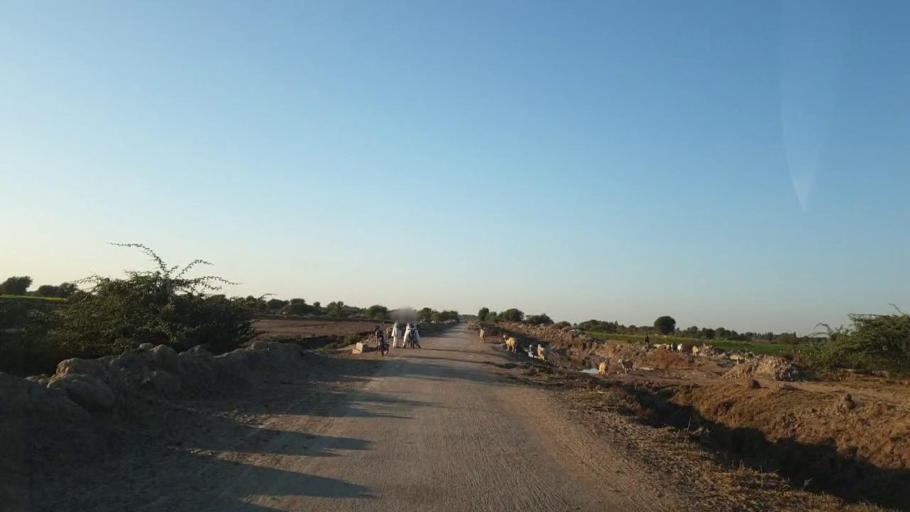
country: PK
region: Sindh
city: Jhol
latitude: 25.8867
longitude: 68.8972
